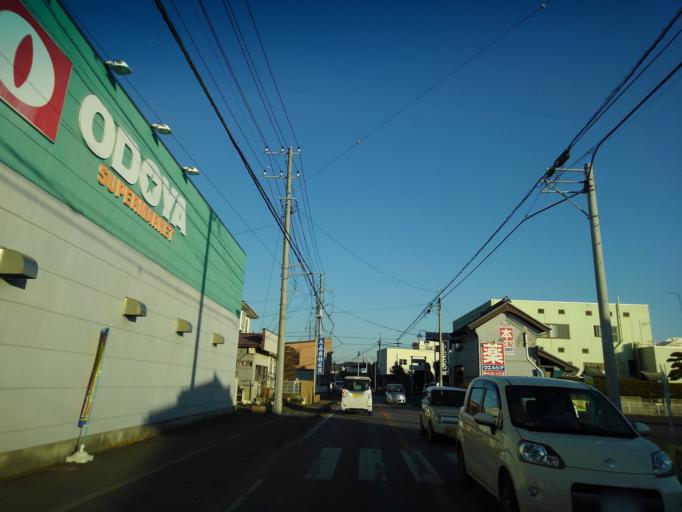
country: JP
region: Chiba
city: Kimitsu
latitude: 35.3056
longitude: 139.9575
